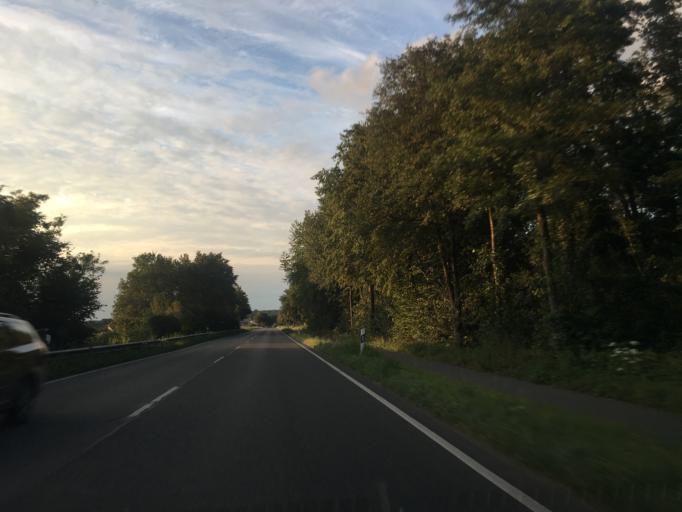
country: DE
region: North Rhine-Westphalia
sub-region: Regierungsbezirk Koln
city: Linnich
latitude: 51.0227
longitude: 6.2761
